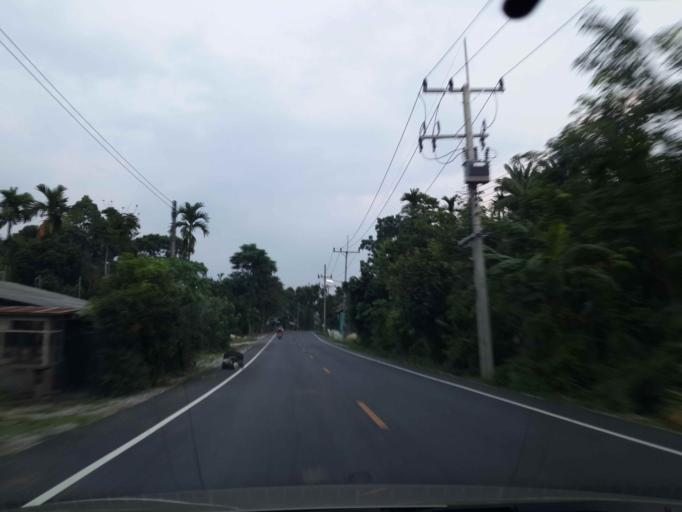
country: TH
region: Narathiwat
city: Rueso
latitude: 6.3492
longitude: 101.4764
